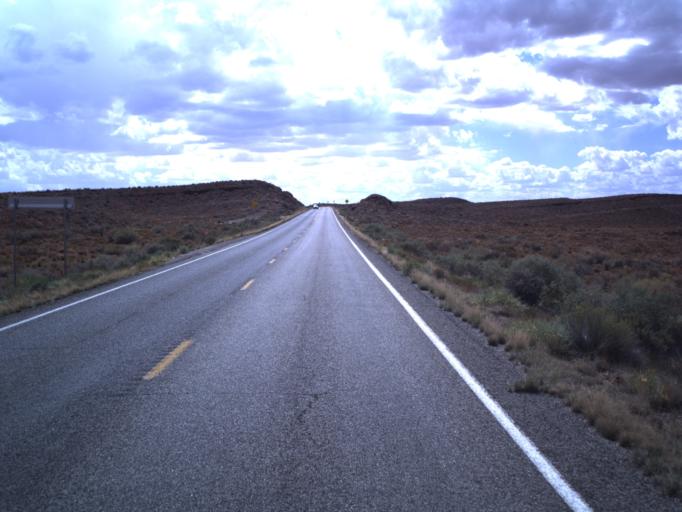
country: US
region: Utah
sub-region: San Juan County
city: Blanding
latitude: 37.1719
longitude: -109.8603
